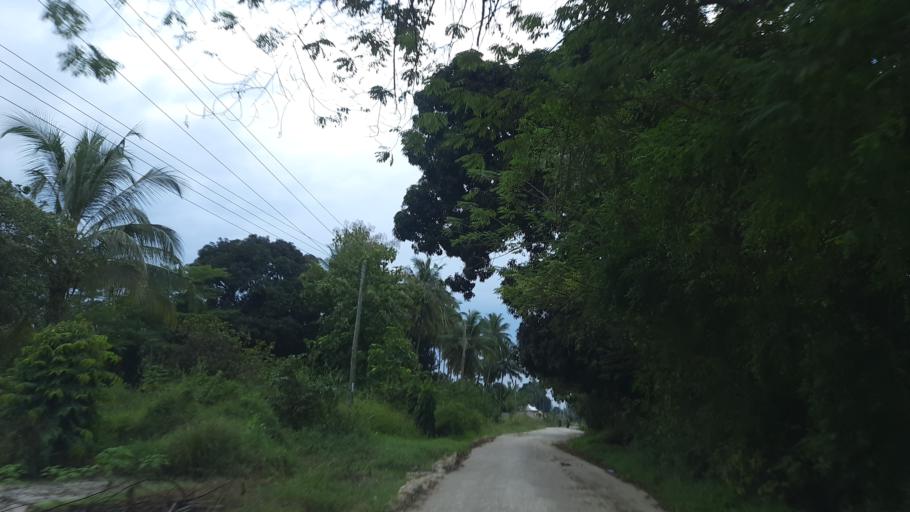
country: TZ
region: Pwani
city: Bagamoyo
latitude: -6.5138
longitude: 38.9301
